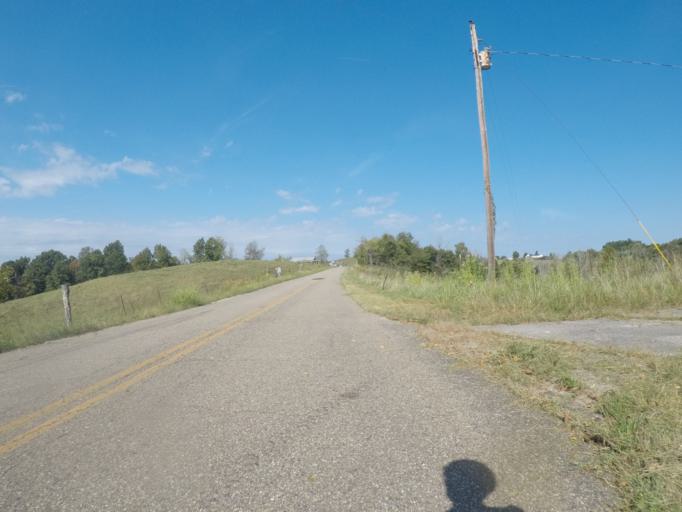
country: US
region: West Virginia
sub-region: Cabell County
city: Lesage
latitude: 38.6446
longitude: -82.4143
